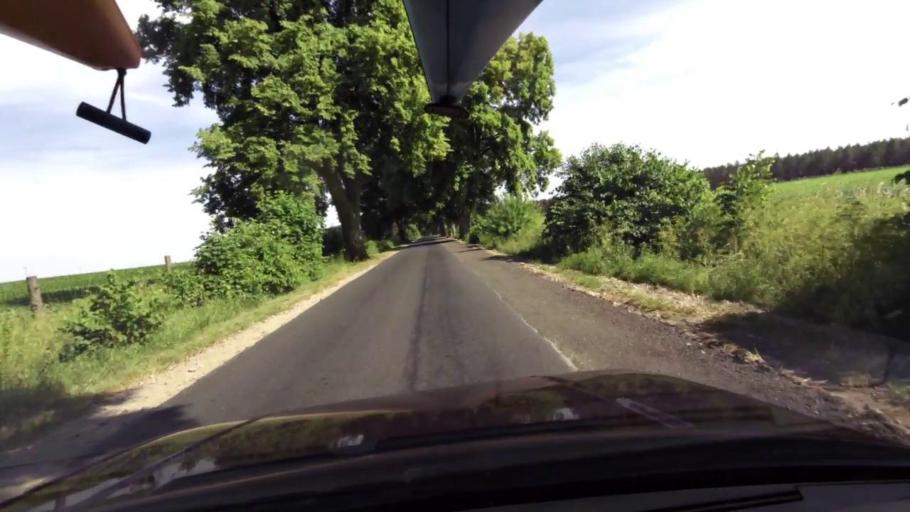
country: PL
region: Pomeranian Voivodeship
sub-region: Powiat bytowski
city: Miastko
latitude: 54.1146
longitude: 16.9537
